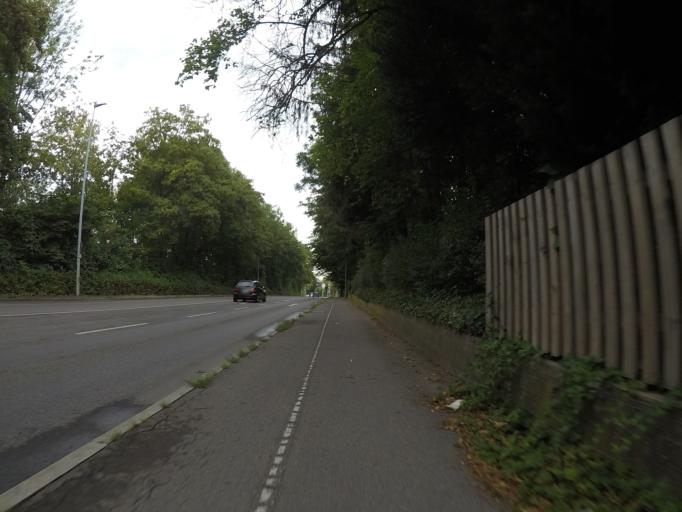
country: DE
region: Baden-Wuerttemberg
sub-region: Tuebingen Region
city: Reutlingen
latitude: 48.4839
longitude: 9.1961
